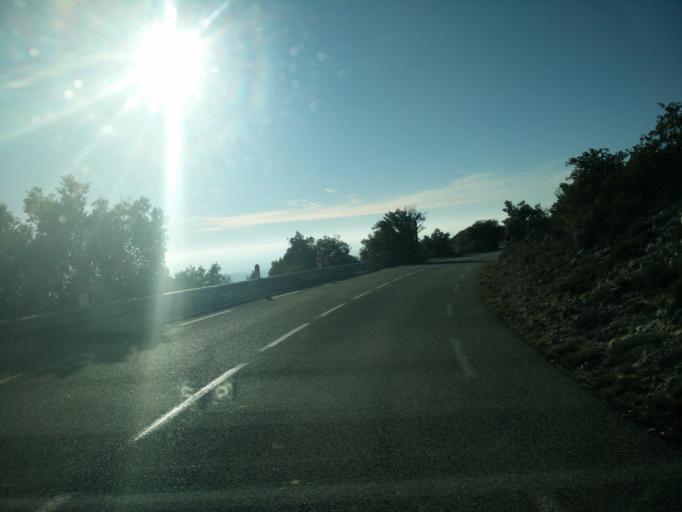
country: FR
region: Provence-Alpes-Cote d'Azur
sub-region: Departement des Alpes-Maritimes
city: Saint-Vallier-de-Thiey
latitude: 43.7044
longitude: 6.8179
